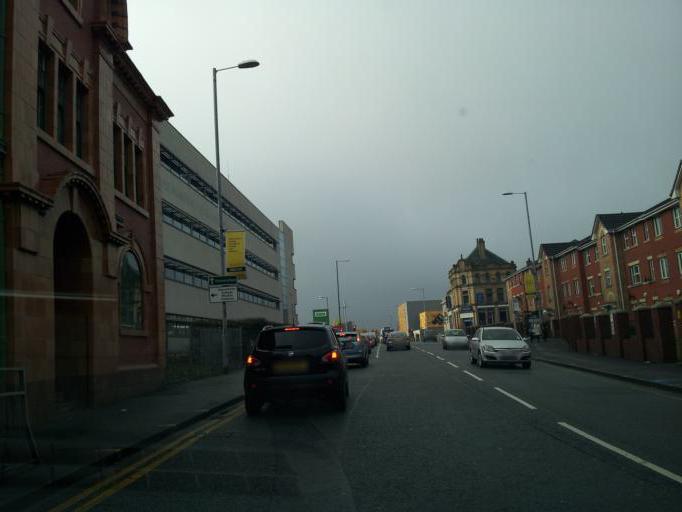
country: GB
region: England
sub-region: Manchester
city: Blackley
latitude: 53.5149
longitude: -2.2126
